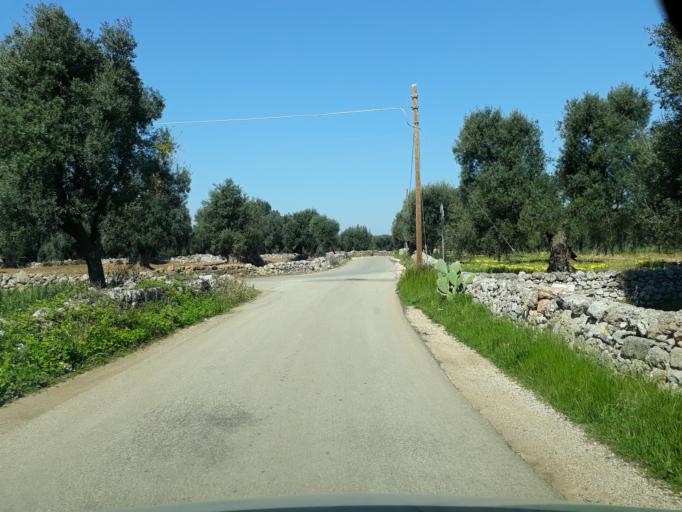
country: IT
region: Apulia
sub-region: Provincia di Brindisi
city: Fasano
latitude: 40.8300
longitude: 17.3791
